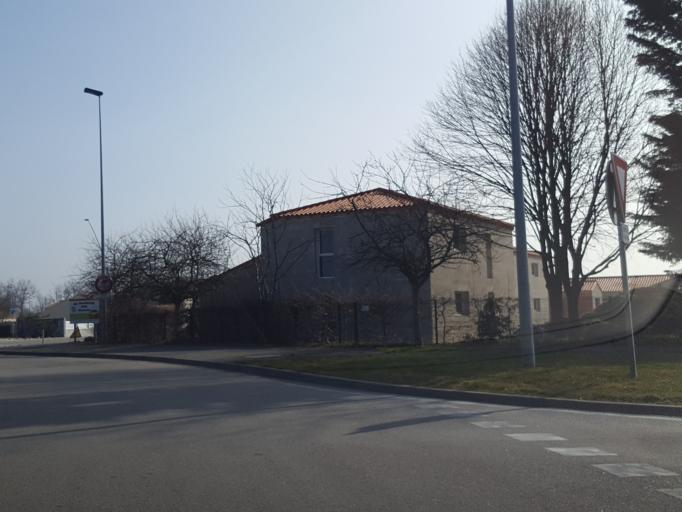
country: FR
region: Pays de la Loire
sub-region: Departement de la Vendee
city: La Roche-sur-Yon
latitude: 46.6832
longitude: -1.4476
